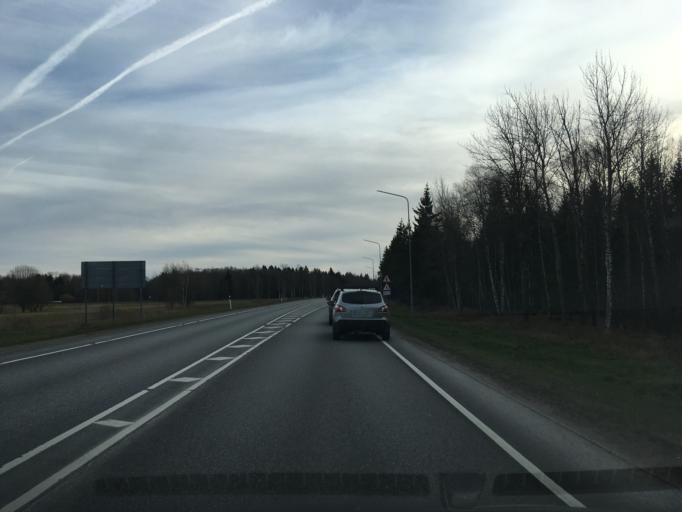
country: EE
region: Ida-Virumaa
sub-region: Kohtla-Jaerve linn
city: Kohtla-Jarve
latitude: 59.4198
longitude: 27.2808
